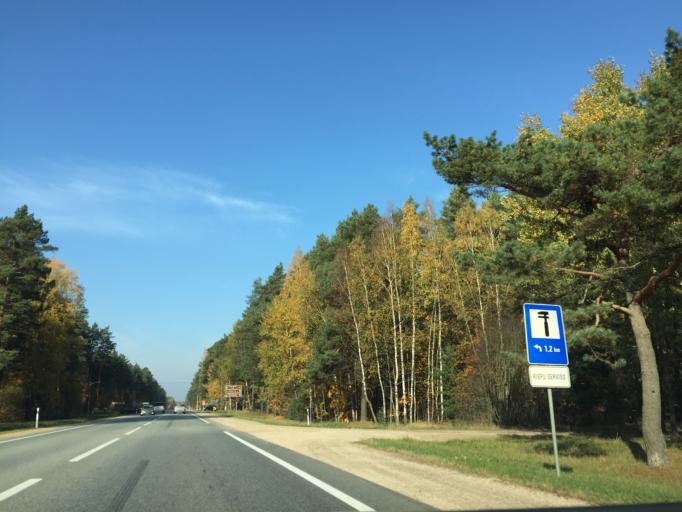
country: LV
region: Babite
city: Pinki
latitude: 56.8849
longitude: 23.9444
